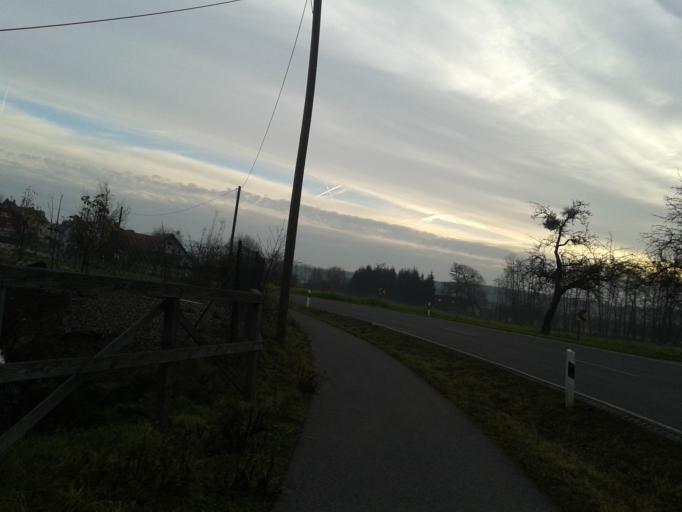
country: DE
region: Bavaria
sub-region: Upper Franconia
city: Memmelsdorf
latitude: 49.9404
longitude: 10.9462
